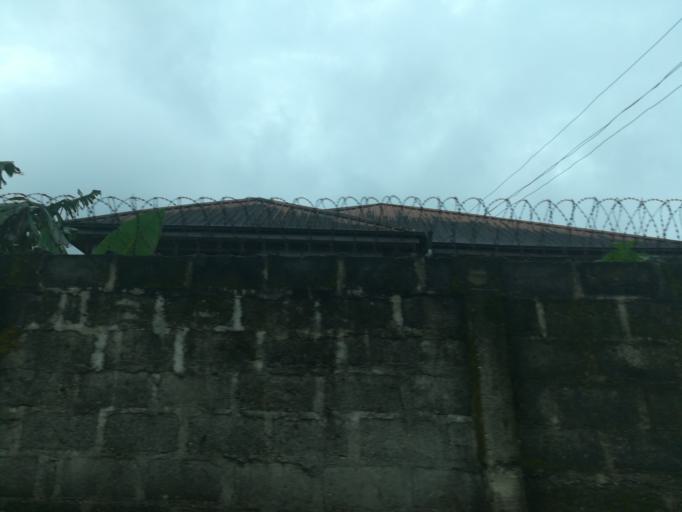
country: NG
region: Rivers
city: Port Harcourt
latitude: 4.8599
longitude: 7.0350
